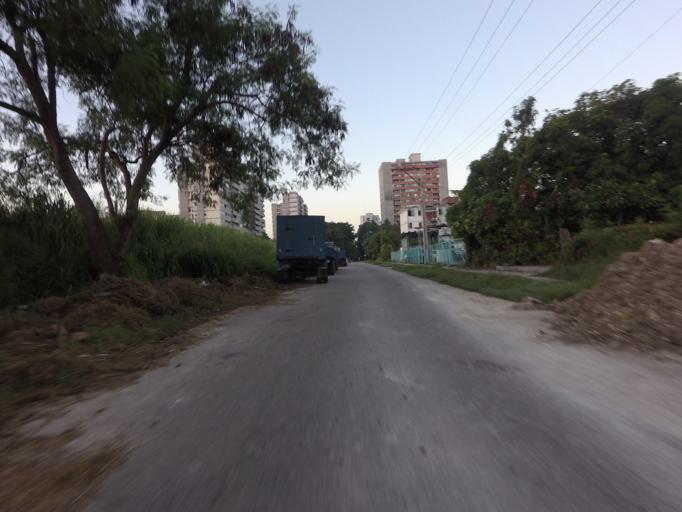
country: CU
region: La Habana
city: Havana
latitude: 23.1214
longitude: -82.3919
